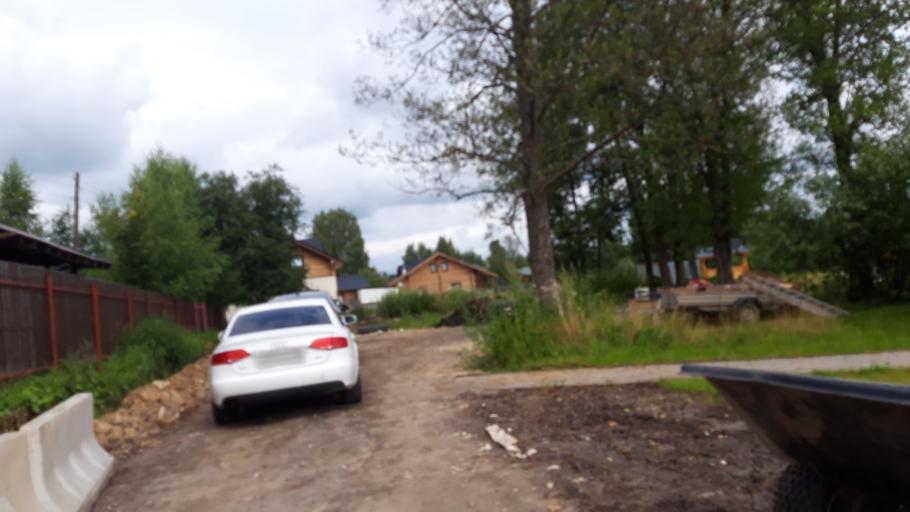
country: RU
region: Tverskaya
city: Konakovo
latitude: 56.6750
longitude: 36.7222
